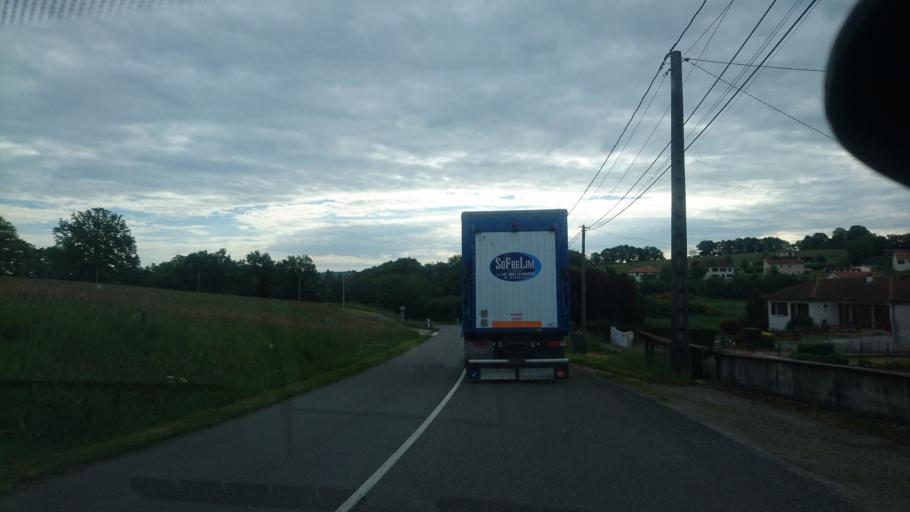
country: FR
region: Limousin
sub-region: Departement de la Haute-Vienne
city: Chateauneuf-la-Foret
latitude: 45.7055
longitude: 1.5934
